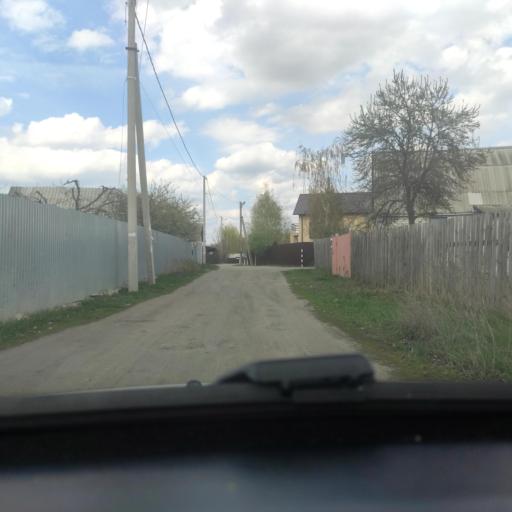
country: RU
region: Voronezj
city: Somovo
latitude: 51.6950
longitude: 39.3687
